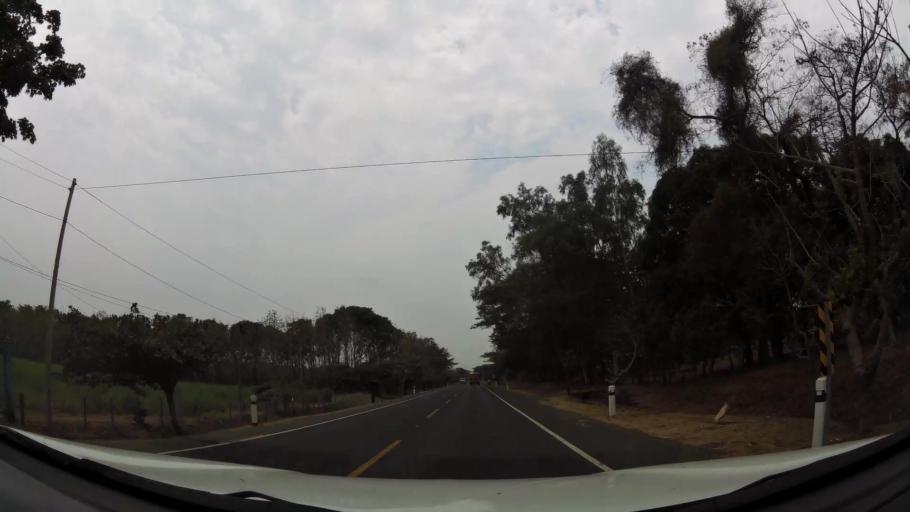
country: NI
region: Chinandega
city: Chichigalpa
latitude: 12.5958
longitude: -87.0328
